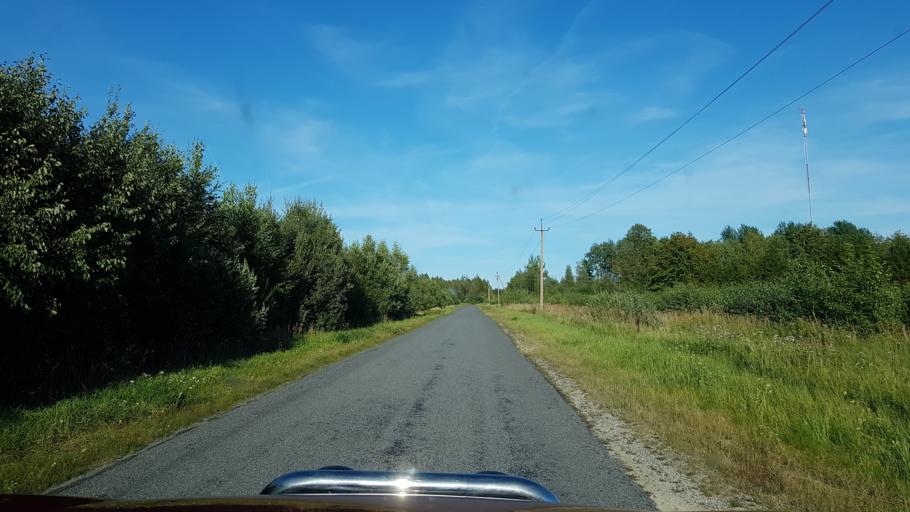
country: LV
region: Salacgrivas
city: Ainazi
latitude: 57.8773
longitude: 24.3770
